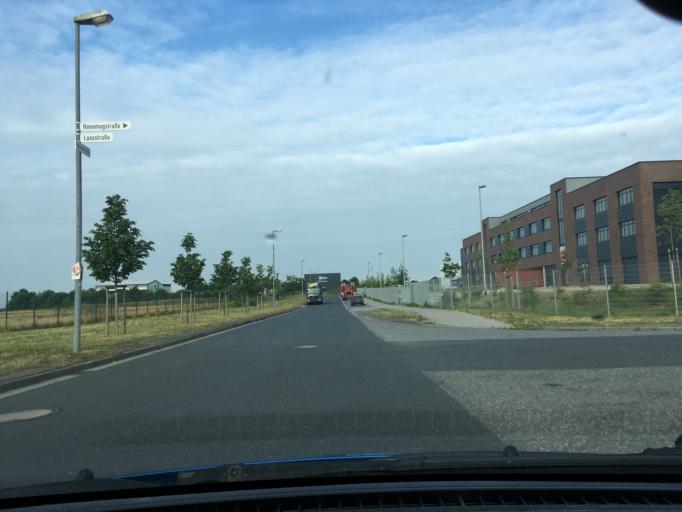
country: DE
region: Lower Saxony
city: Buchholz in der Nordheide
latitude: 53.3244
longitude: 9.8189
